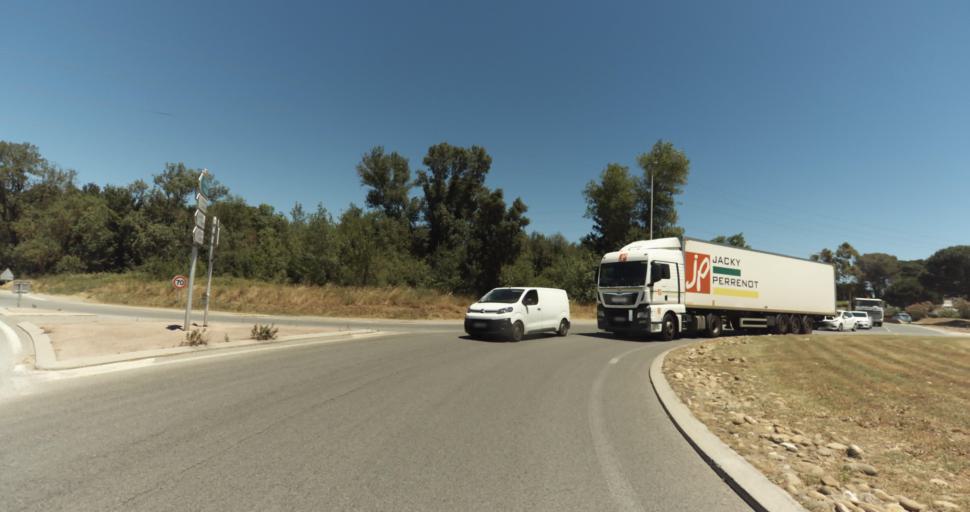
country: FR
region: Provence-Alpes-Cote d'Azur
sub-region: Departement du Var
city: Gassin
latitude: 43.2602
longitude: 6.5685
